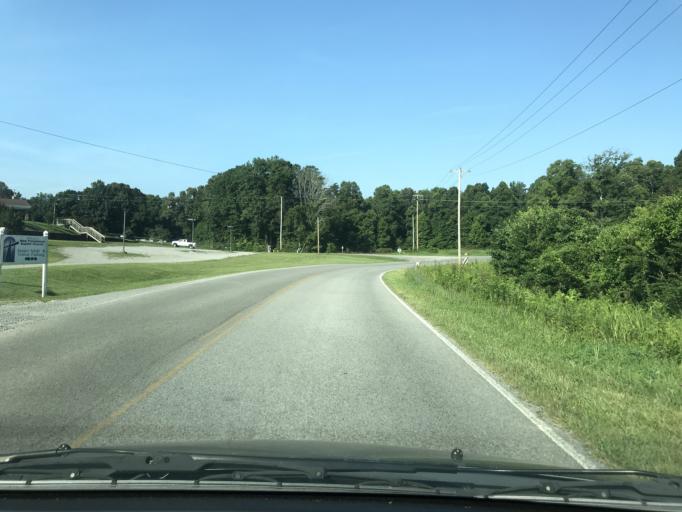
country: US
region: Tennessee
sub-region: Loudon County
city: Loudon
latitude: 35.7788
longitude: -84.3518
